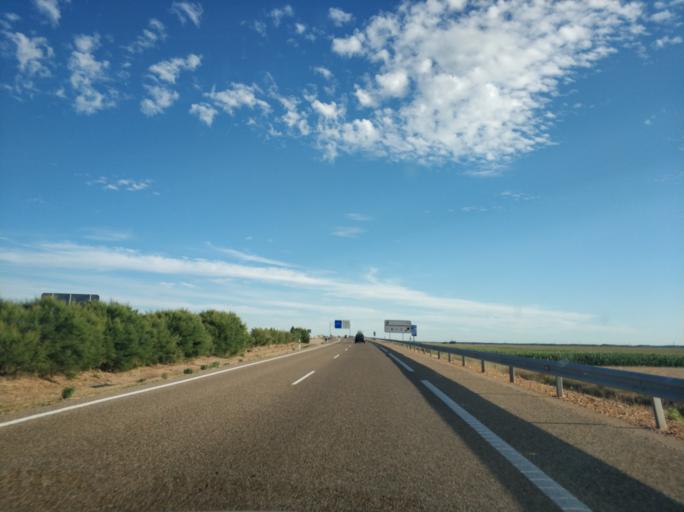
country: ES
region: Castille and Leon
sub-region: Provincia de Leon
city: Villamanan
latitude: 42.3349
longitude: -5.6093
